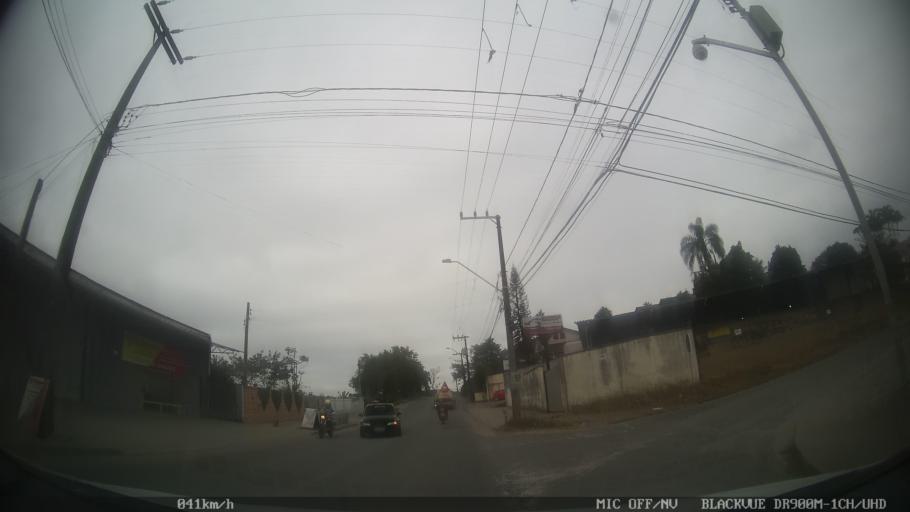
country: BR
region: Santa Catarina
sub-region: Joinville
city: Joinville
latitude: -26.3327
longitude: -48.8057
